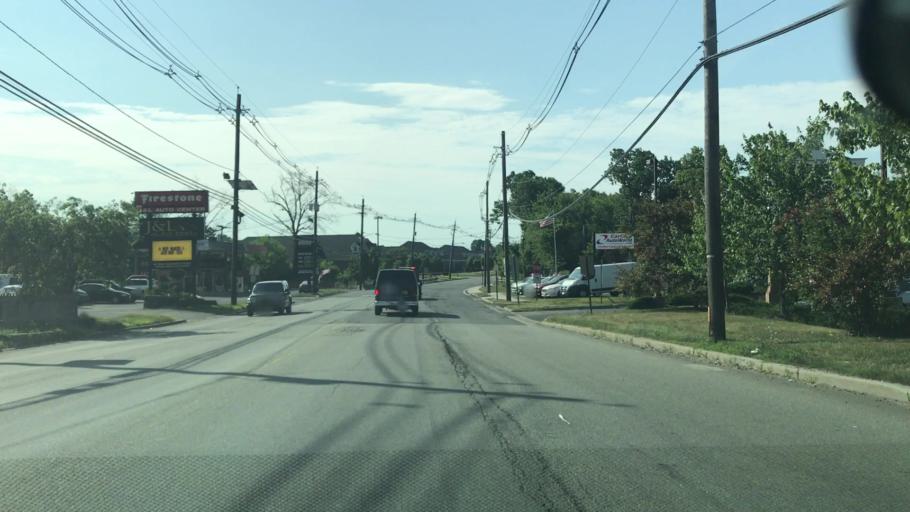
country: US
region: New Jersey
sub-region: Middlesex County
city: South Plainfield
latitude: 40.5588
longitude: -74.4172
